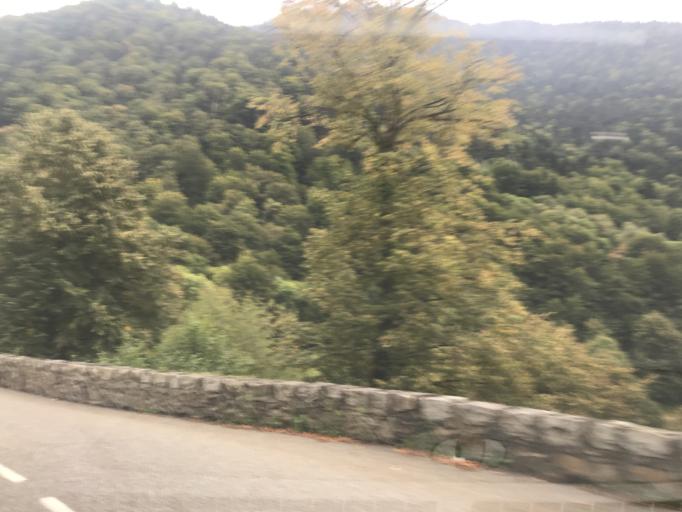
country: FR
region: Midi-Pyrenees
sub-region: Departement de la Haute-Garonne
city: Bagneres-de-Luchon
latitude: 42.7702
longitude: 0.6205
